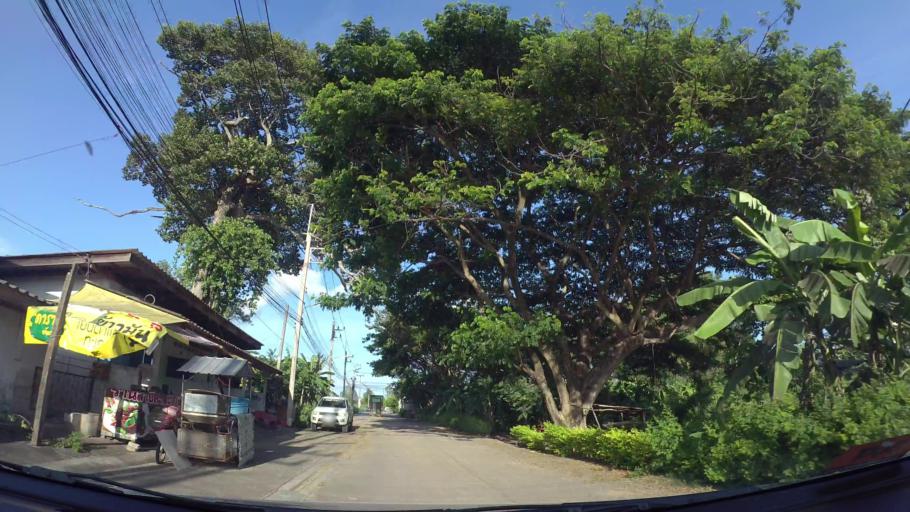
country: TH
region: Rayong
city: Rayong
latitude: 12.6845
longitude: 101.2904
